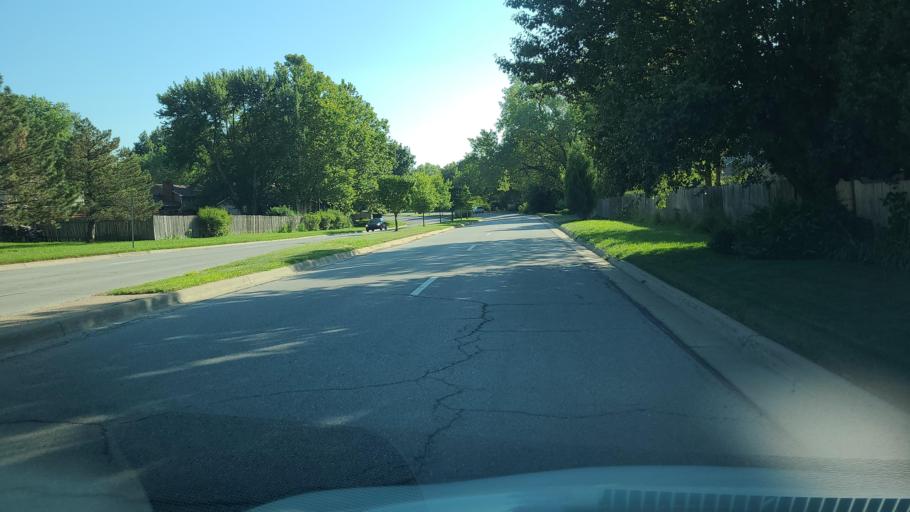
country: US
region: Kansas
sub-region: Douglas County
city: Lawrence
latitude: 38.9774
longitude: -95.2798
